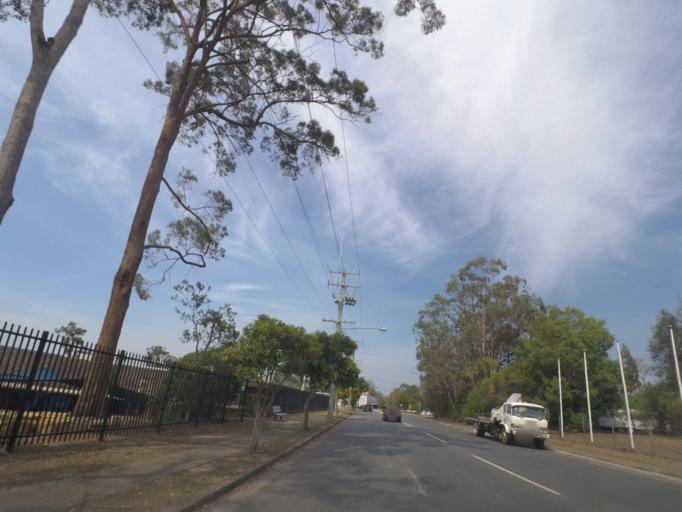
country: AU
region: Queensland
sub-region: Brisbane
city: Sunnybank
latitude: -27.5978
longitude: 153.0431
